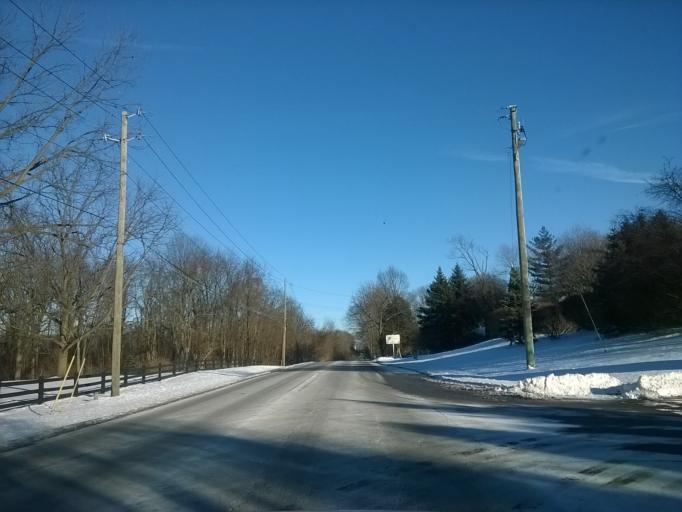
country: US
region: Indiana
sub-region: Marion County
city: Meridian Hills
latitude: 39.9269
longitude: -86.1756
